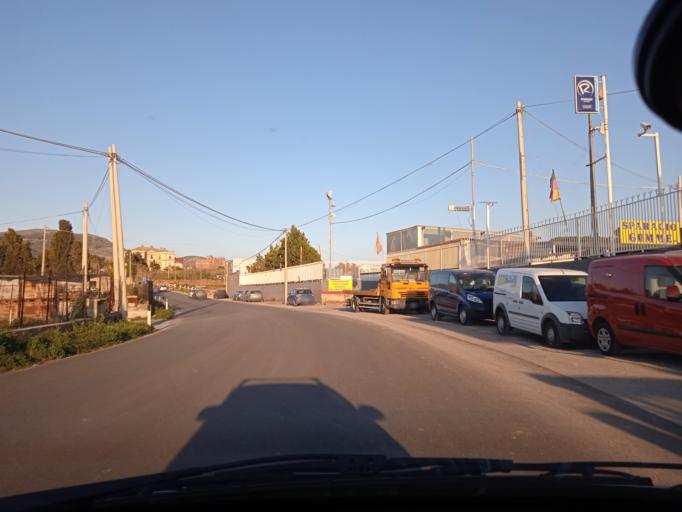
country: IT
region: Sicily
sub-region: Palermo
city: Bagheria
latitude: 38.0886
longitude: 13.4959
